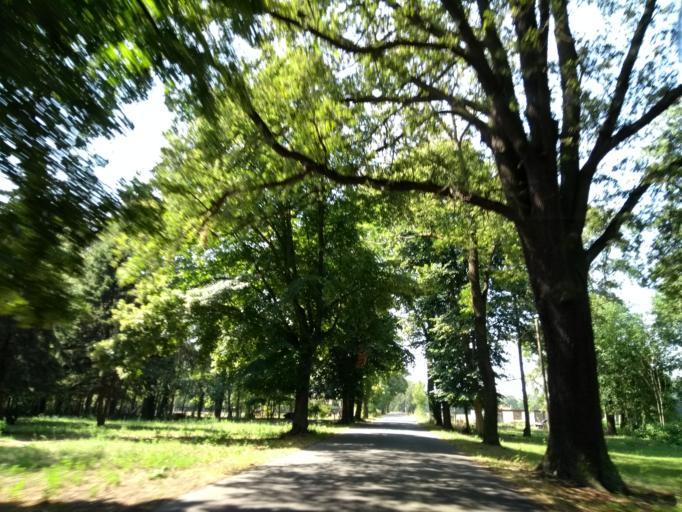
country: DE
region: Brandenburg
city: Burg
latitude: 51.8442
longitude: 14.1407
